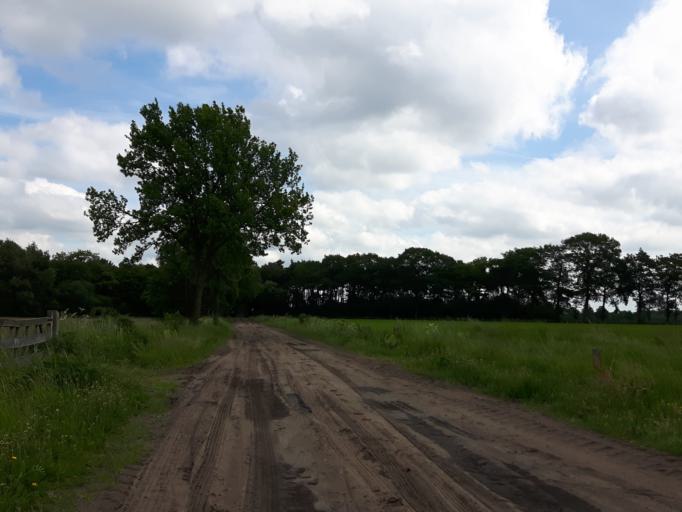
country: NL
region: Overijssel
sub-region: Gemeente Enschede
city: Enschede
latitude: 52.1752
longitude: 6.8435
